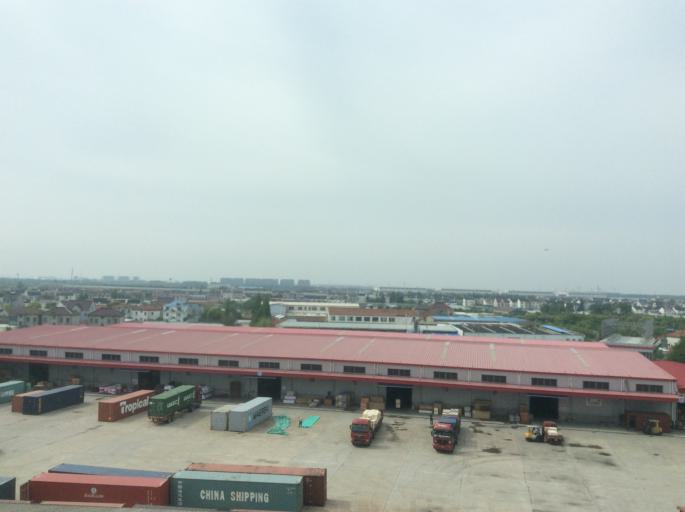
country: CN
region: Shanghai Shi
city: Kangqiao
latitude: 31.2093
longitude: 121.7417
